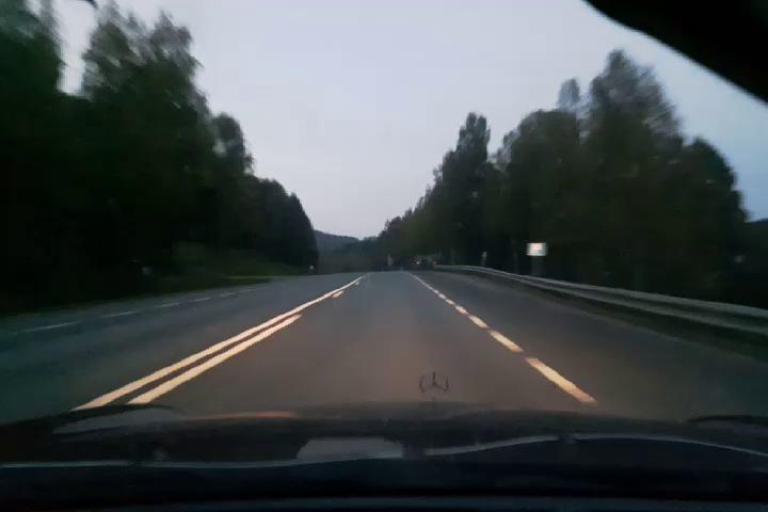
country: SE
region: Vaesternorrland
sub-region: Kramfors Kommun
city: Nordingra
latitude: 63.0183
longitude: 18.2949
